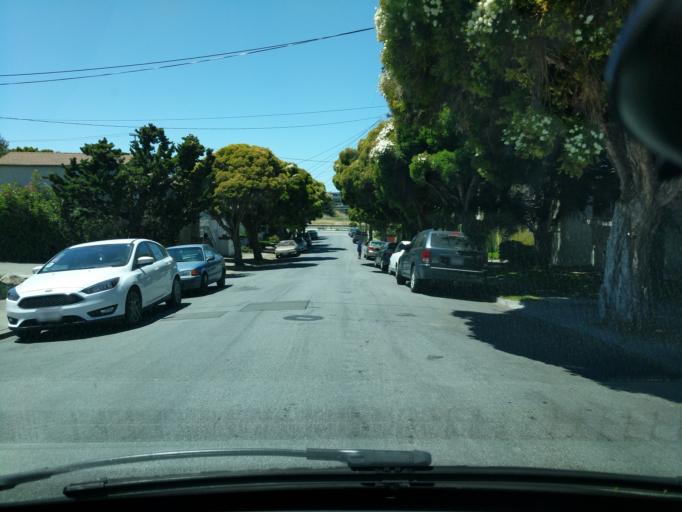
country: US
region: California
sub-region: Alameda County
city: Albany
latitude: 37.8882
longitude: -122.3058
